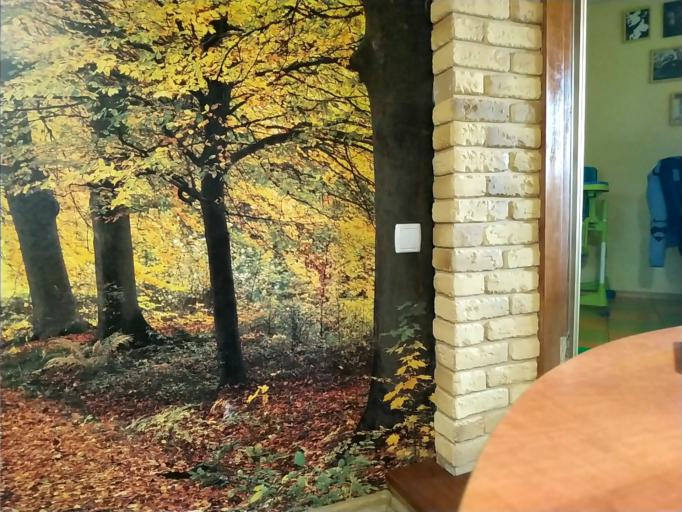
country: RU
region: Leningrad
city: Tolmachevo
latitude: 58.9453
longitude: 29.6540
